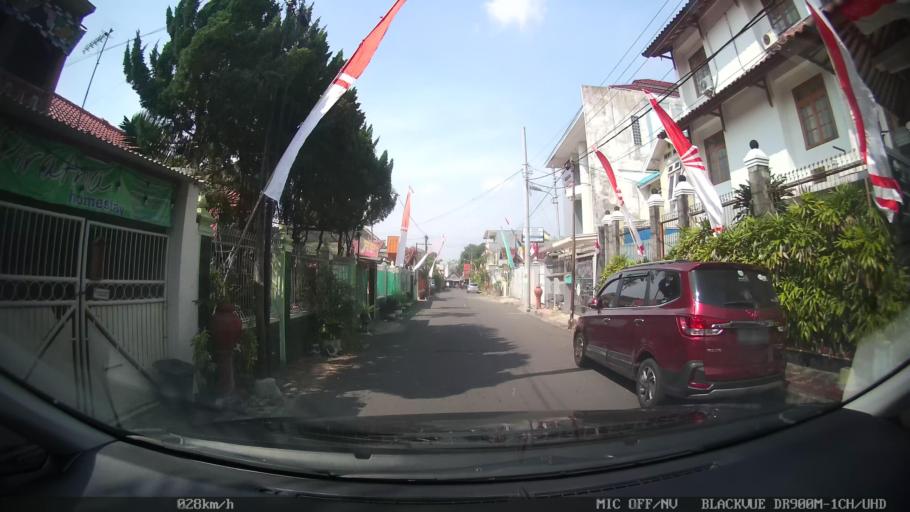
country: ID
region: Daerah Istimewa Yogyakarta
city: Yogyakarta
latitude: -7.7923
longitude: 110.3603
